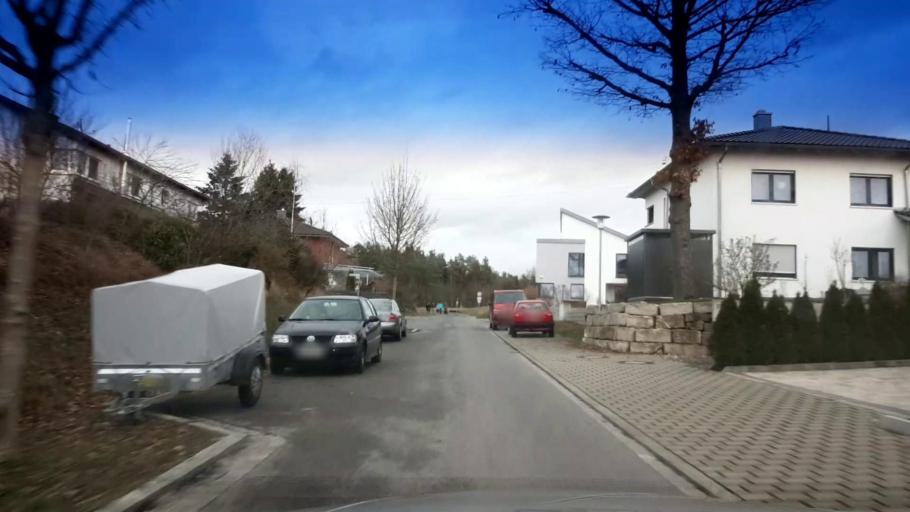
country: DE
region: Bavaria
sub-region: Upper Franconia
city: Breitengussbach
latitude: 49.9668
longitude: 10.8922
